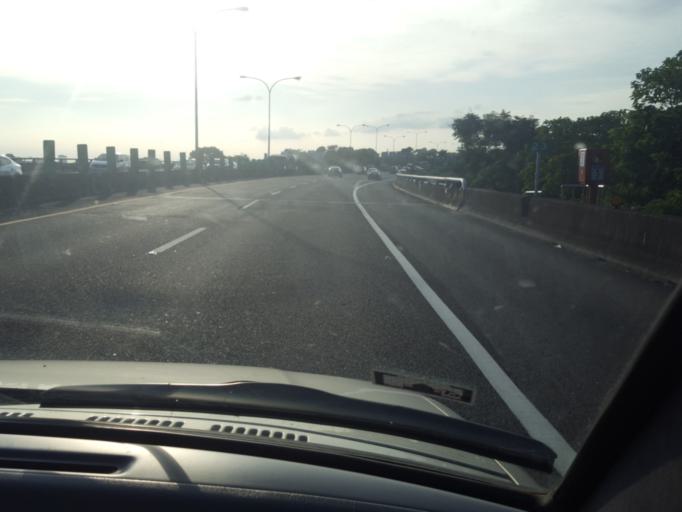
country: TW
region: Taipei
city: Taipei
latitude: 25.0730
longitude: 121.5356
